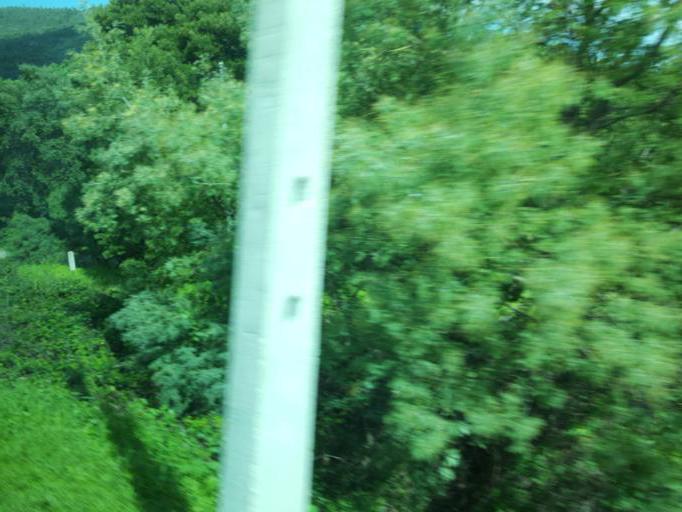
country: PT
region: Faro
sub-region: Monchique
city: Monchique
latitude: 37.2845
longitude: -8.5573
